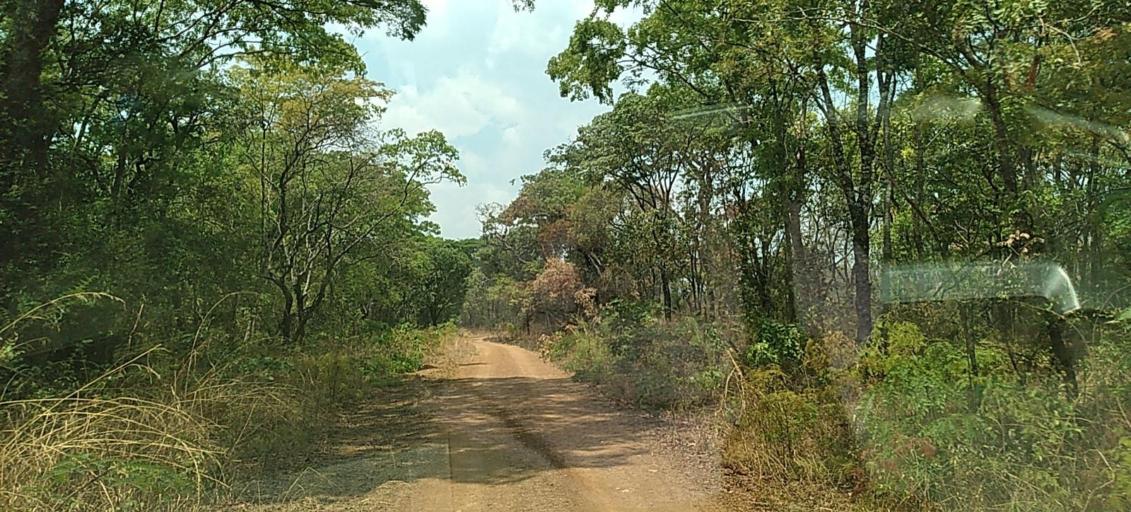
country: ZM
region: Copperbelt
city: Chingola
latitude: -12.7896
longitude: 27.6509
